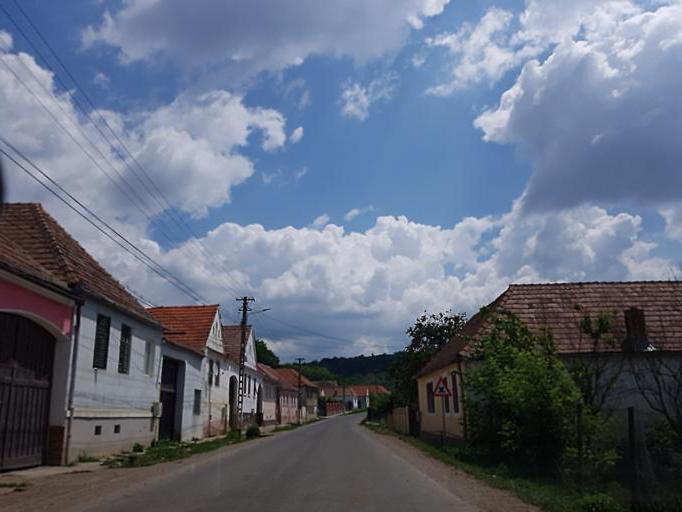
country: RO
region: Sibiu
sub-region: Comuna Seica Mica
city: Seica Mica
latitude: 46.0531
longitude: 24.1395
